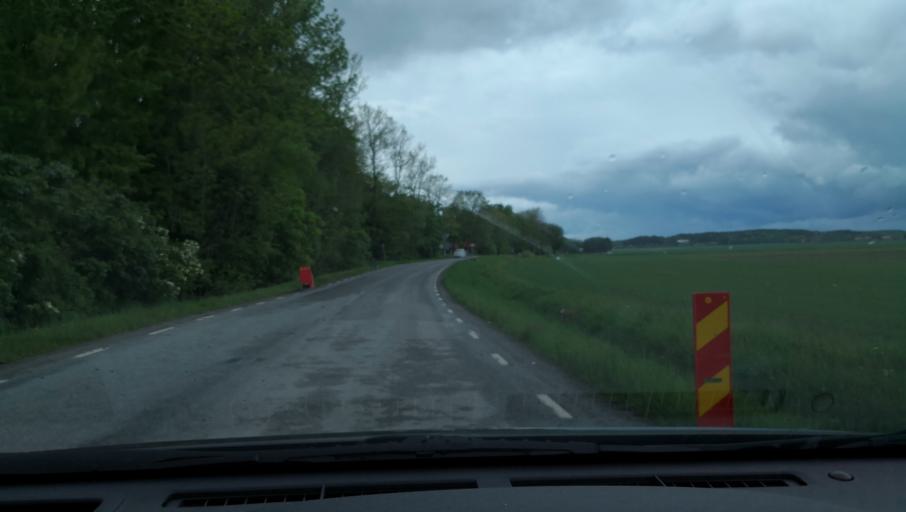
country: SE
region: Uppsala
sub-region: Enkopings Kommun
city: Orsundsbro
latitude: 59.7217
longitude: 17.3371
